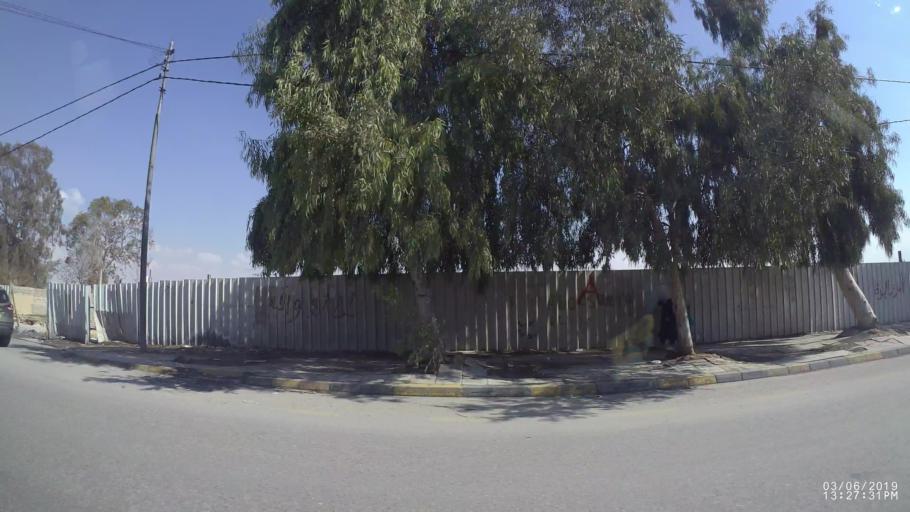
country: JO
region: Zarqa
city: Zarqa
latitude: 32.0695
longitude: 36.0977
